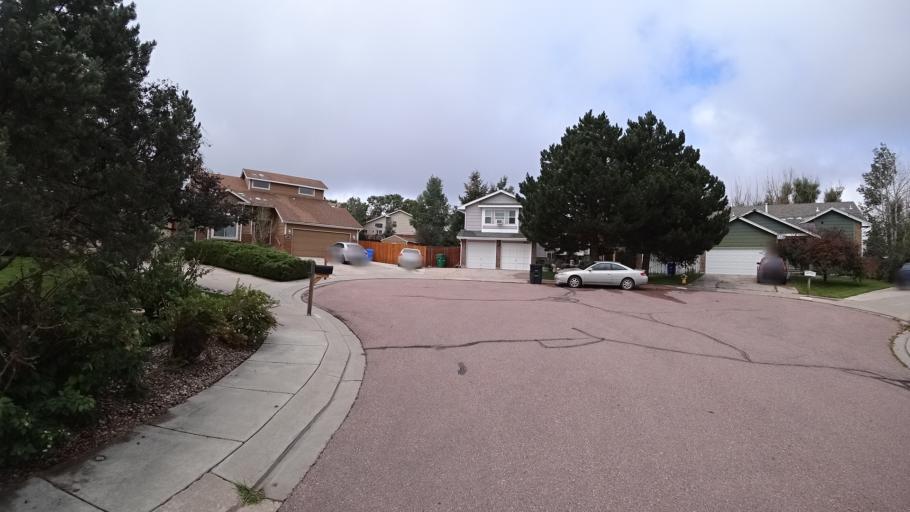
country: US
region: Colorado
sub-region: El Paso County
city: Cimarron Hills
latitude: 38.9225
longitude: -104.7633
